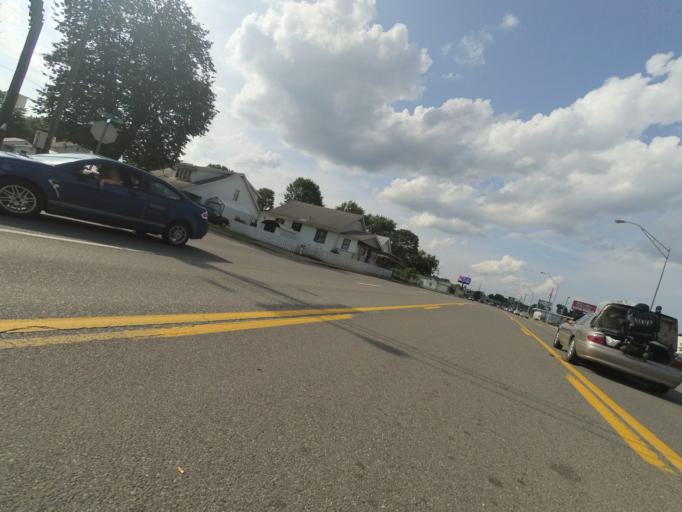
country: US
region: West Virginia
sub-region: Cabell County
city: Huntington
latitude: 38.4252
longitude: -82.3929
